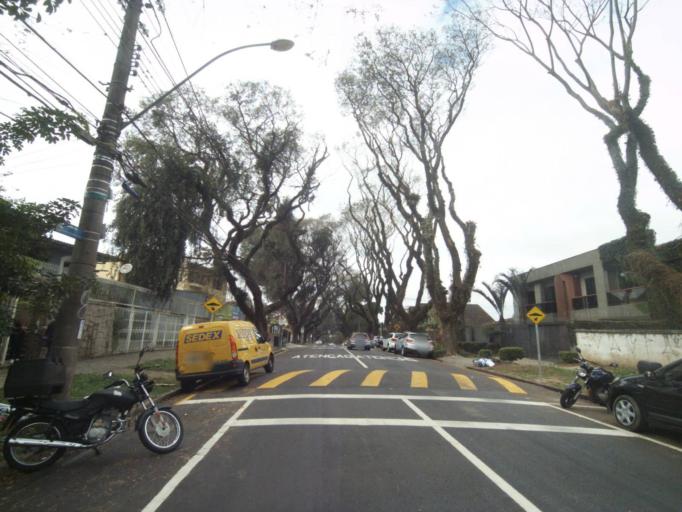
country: BR
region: Parana
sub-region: Curitiba
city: Curitiba
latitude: -25.4491
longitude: -49.3106
